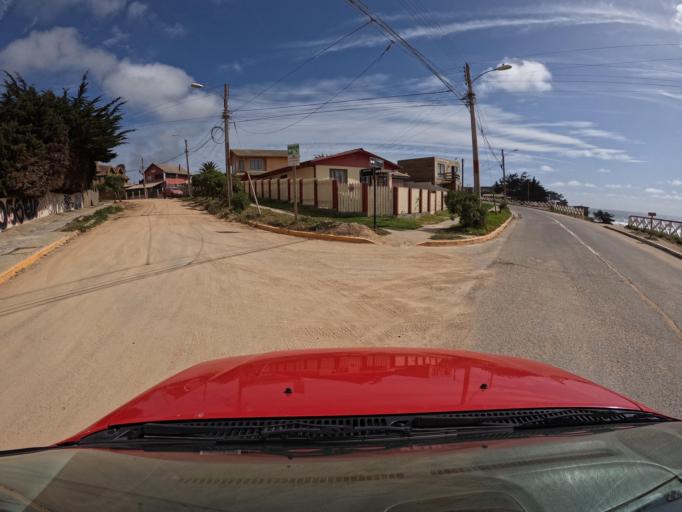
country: CL
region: O'Higgins
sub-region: Provincia de Colchagua
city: Santa Cruz
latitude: -34.3895
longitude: -72.0203
